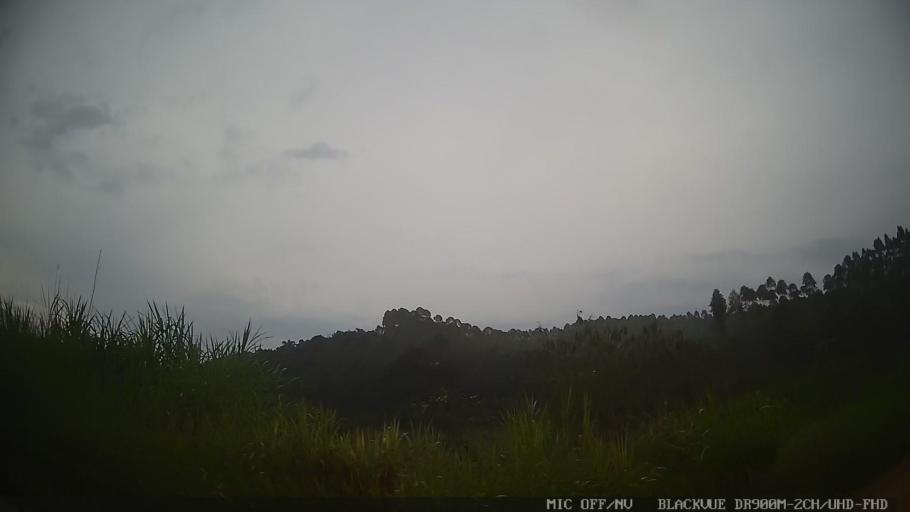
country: BR
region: Sao Paulo
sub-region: Suzano
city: Suzano
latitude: -23.6577
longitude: -46.2578
